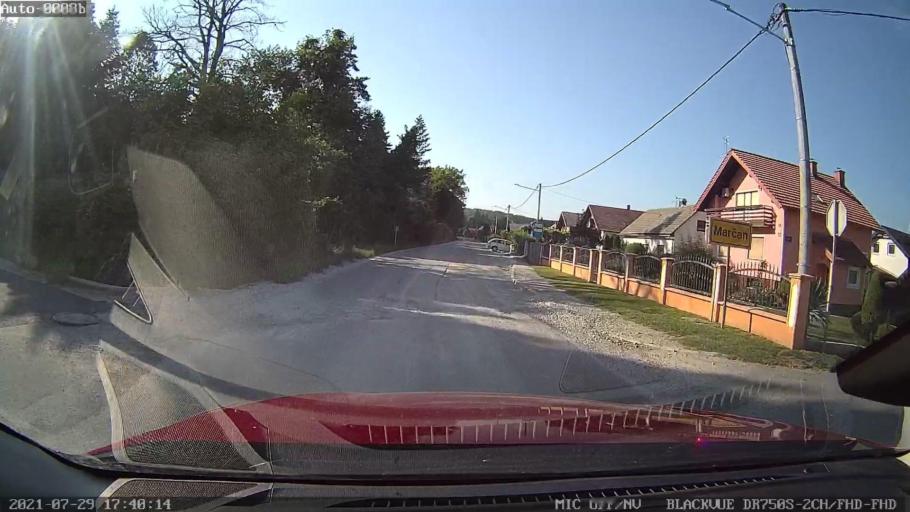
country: HR
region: Varazdinska
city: Vinica
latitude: 46.3210
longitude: 16.1554
